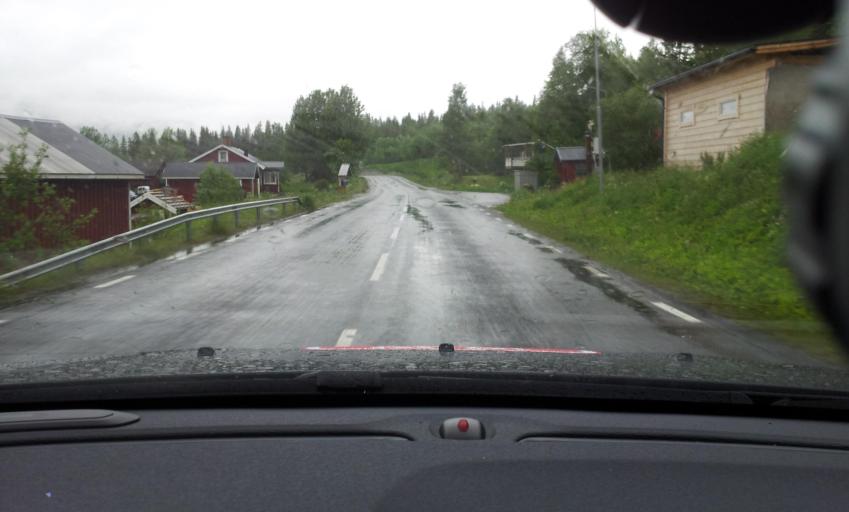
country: SE
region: Jaemtland
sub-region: Are Kommun
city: Are
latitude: 63.2169
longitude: 13.0461
